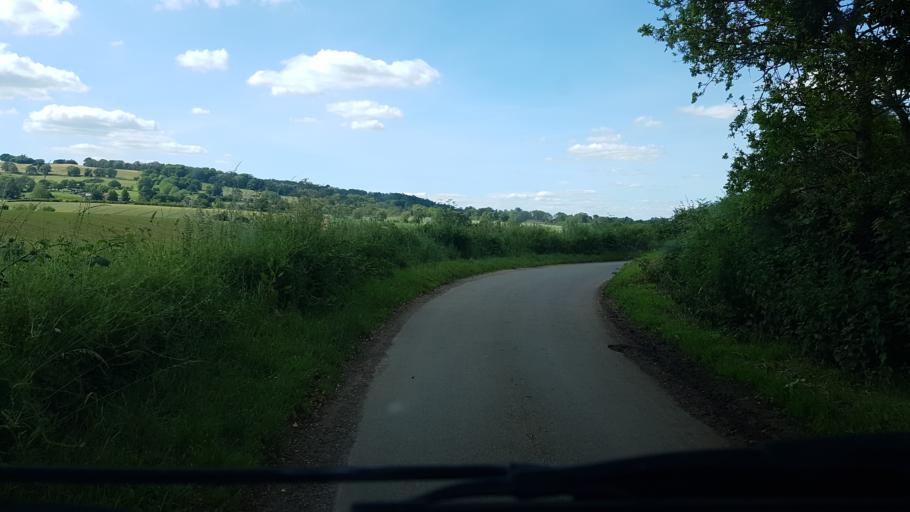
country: GB
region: England
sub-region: Shropshire
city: Romsley
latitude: 52.4543
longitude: -2.2514
